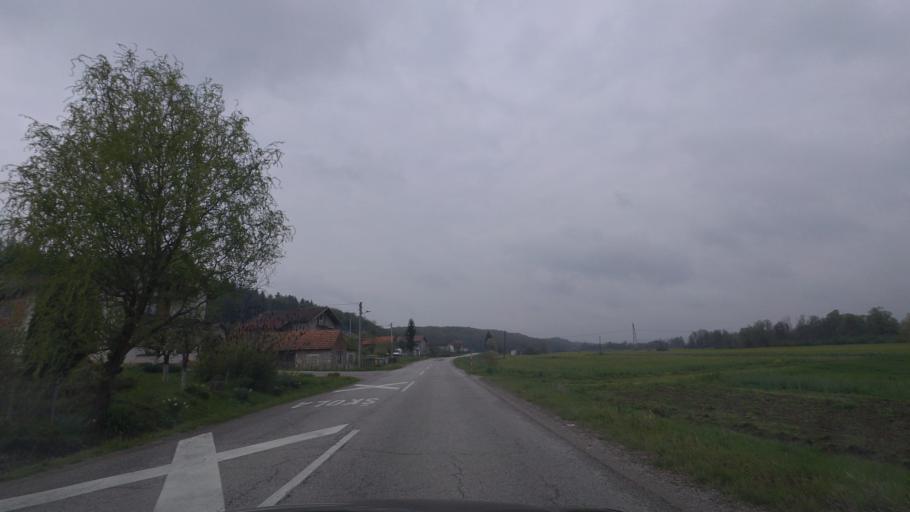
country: HR
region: Zagrebacka
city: Jastrebarsko
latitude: 45.6207
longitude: 15.5661
